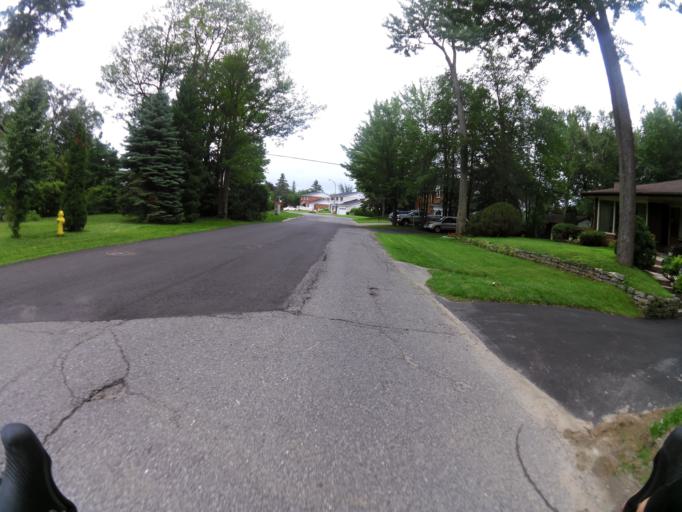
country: CA
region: Ontario
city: Ottawa
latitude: 45.3238
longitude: -75.7090
